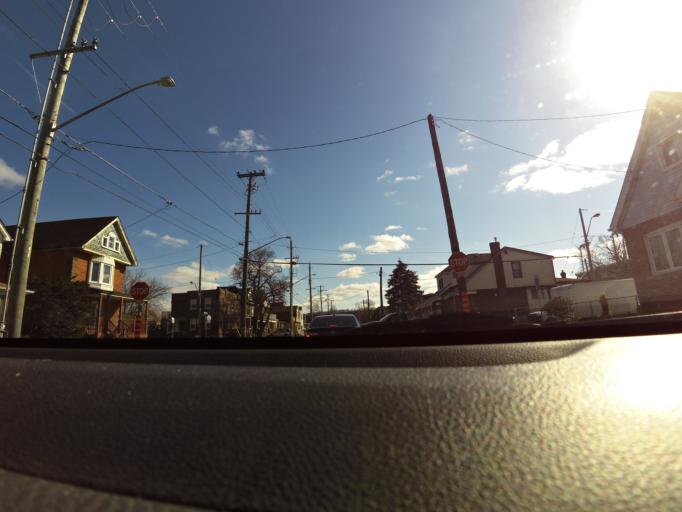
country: CA
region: Ontario
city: Hamilton
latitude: 43.2530
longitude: -79.8263
